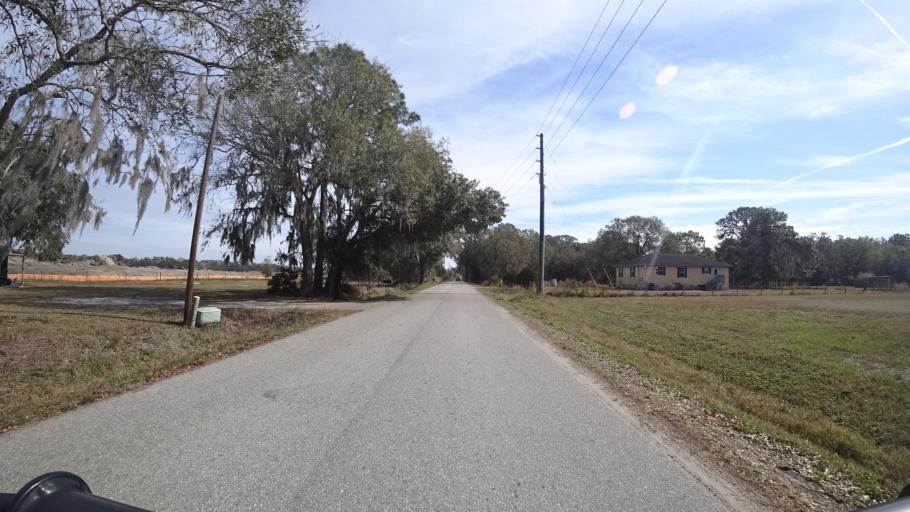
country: US
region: Florida
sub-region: Manatee County
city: Ellenton
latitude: 27.5762
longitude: -82.4414
